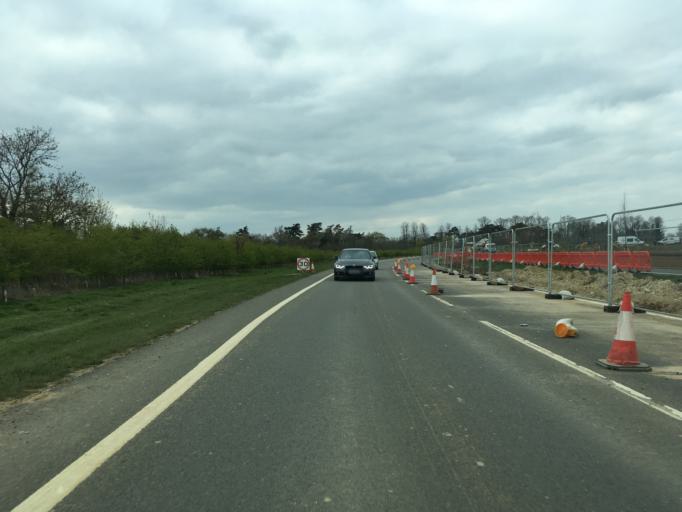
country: GB
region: England
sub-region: Oxfordshire
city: Bicester
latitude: 51.8950
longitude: -1.1822
